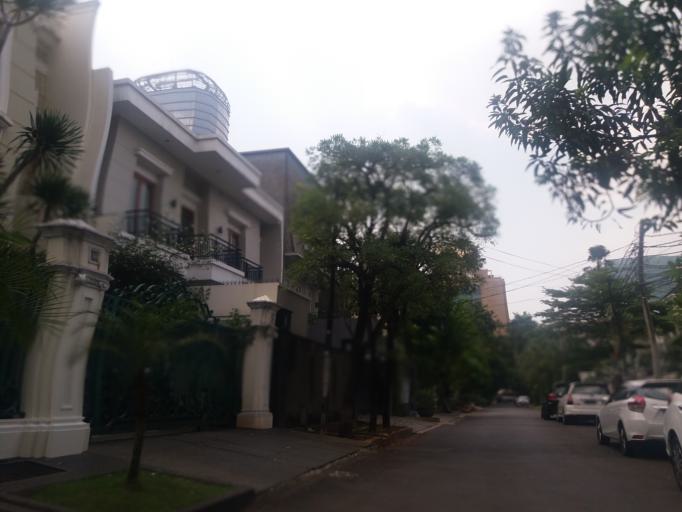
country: ID
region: Jakarta Raya
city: Jakarta
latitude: -6.2286
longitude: 106.8306
